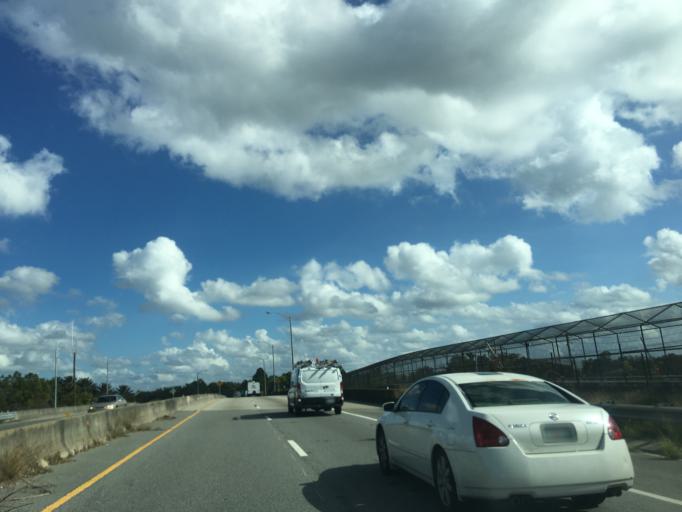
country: US
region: Florida
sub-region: Orange County
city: Maitland
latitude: 28.6370
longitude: -81.3609
